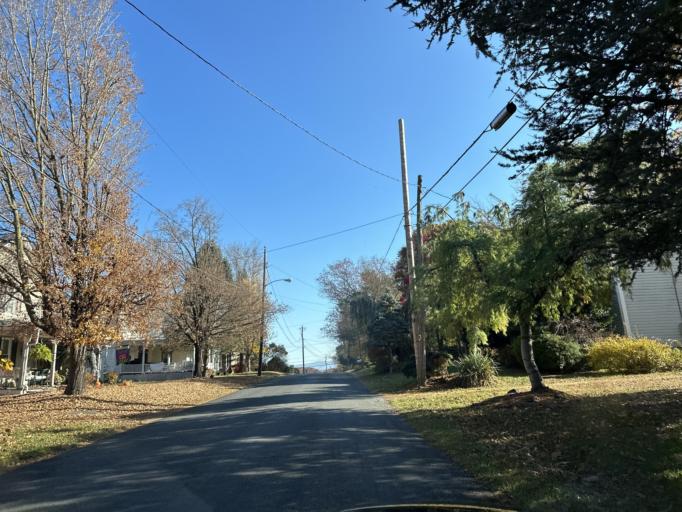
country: US
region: Virginia
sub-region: Augusta County
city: Weyers Cave
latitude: 38.2881
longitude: -78.9103
